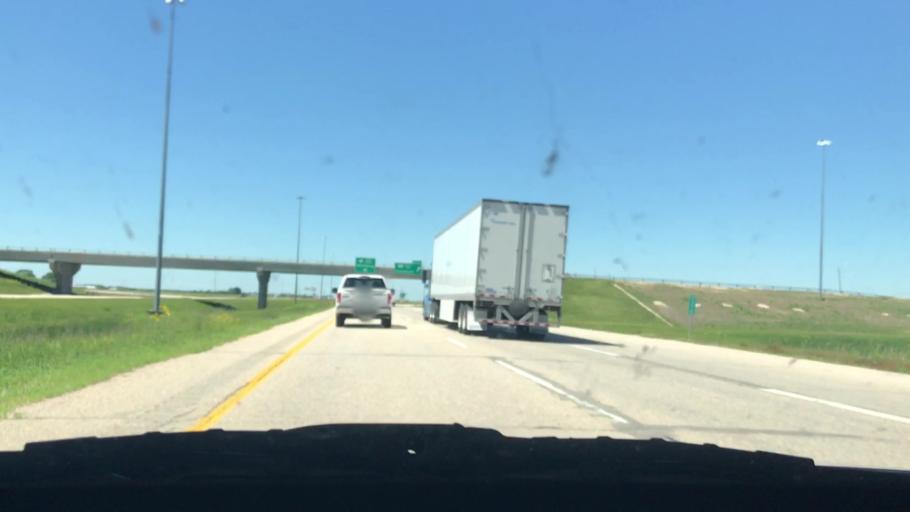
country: CA
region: Manitoba
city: Steinbach
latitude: 49.7009
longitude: -96.6455
